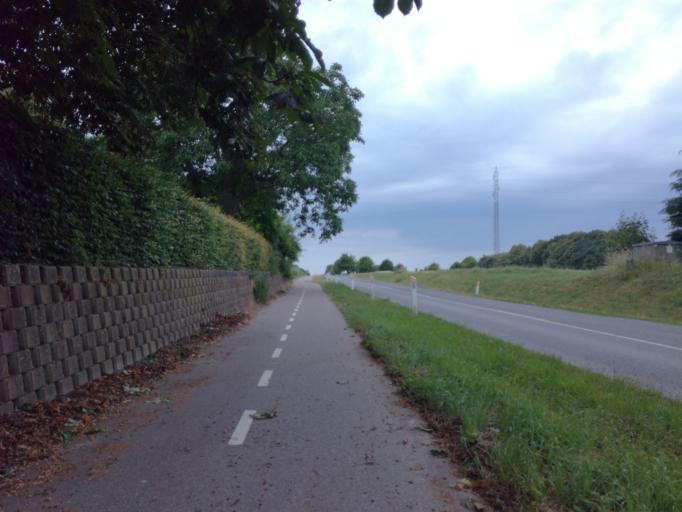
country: DK
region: South Denmark
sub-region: Vejle Kommune
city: Borkop
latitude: 55.6587
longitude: 9.6329
